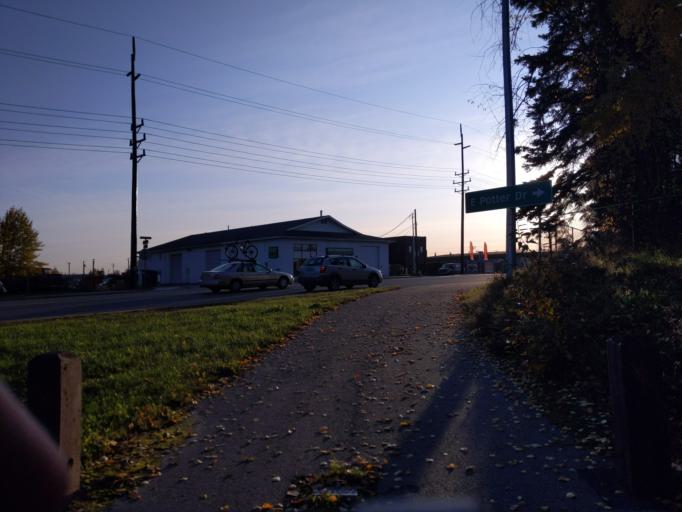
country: US
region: Alaska
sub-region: Anchorage Municipality
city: Anchorage
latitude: 61.1666
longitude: -149.8786
